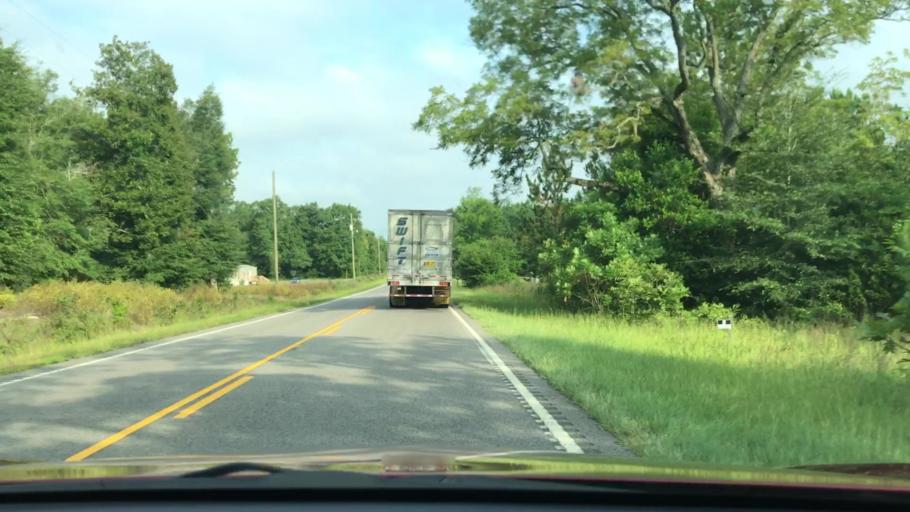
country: US
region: South Carolina
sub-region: Barnwell County
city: Williston
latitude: 33.6312
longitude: -81.3076
